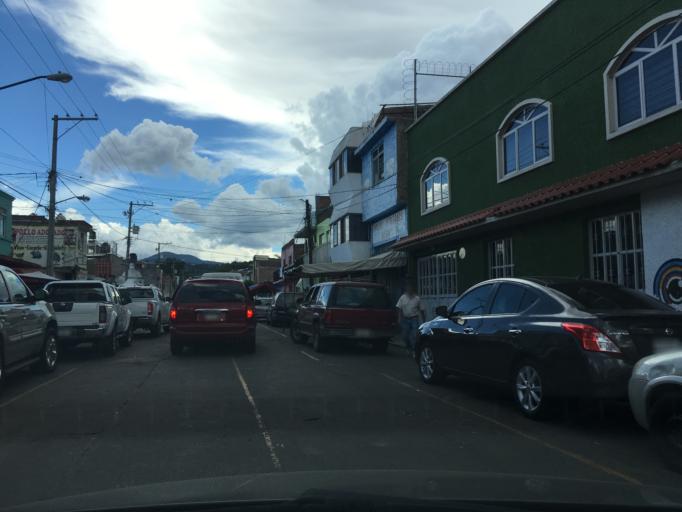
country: MX
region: Michoacan
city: Morelia
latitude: 19.6936
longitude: -101.1926
